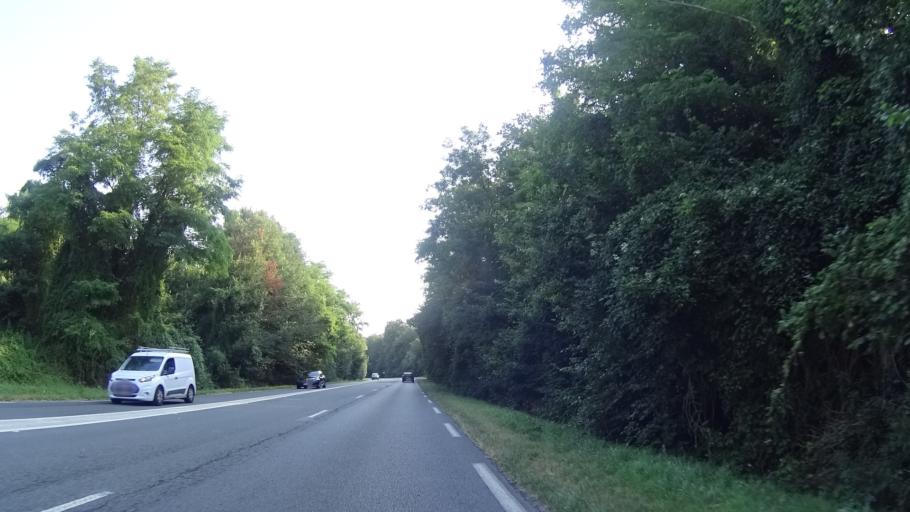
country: FR
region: Ile-de-France
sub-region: Departement du Val-d'Oise
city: Chaumontel
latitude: 49.1330
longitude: 2.4346
